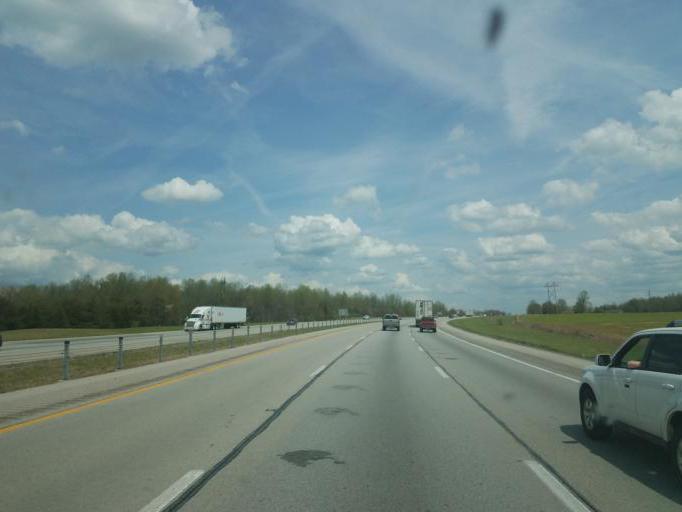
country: US
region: Kentucky
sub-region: Hardin County
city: Elizabethtown
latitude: 37.7205
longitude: -85.8285
